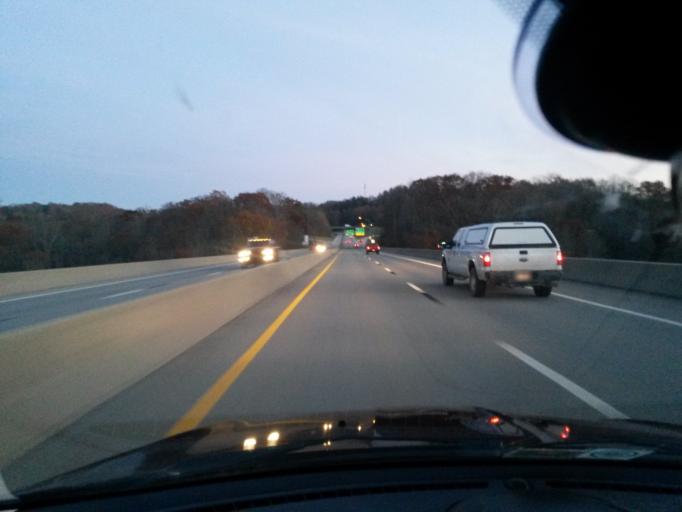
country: US
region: West Virginia
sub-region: Raleigh County
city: Beaver
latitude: 37.7659
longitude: -81.1533
